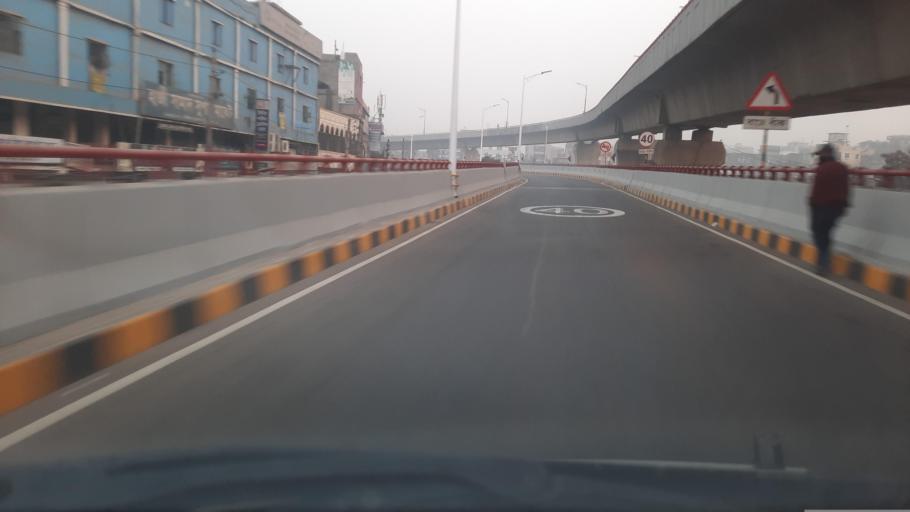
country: BD
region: Dhaka
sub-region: Dhaka
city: Dhaka
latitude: 23.7087
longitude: 90.4345
